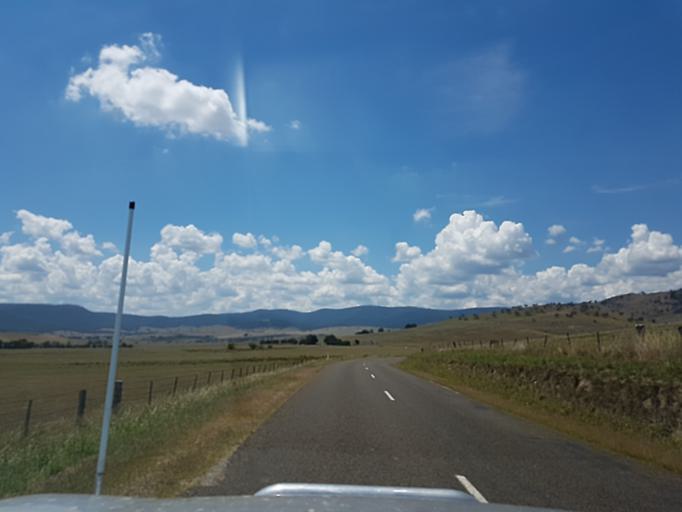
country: AU
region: Victoria
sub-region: Alpine
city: Mount Beauty
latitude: -36.9575
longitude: 147.7576
